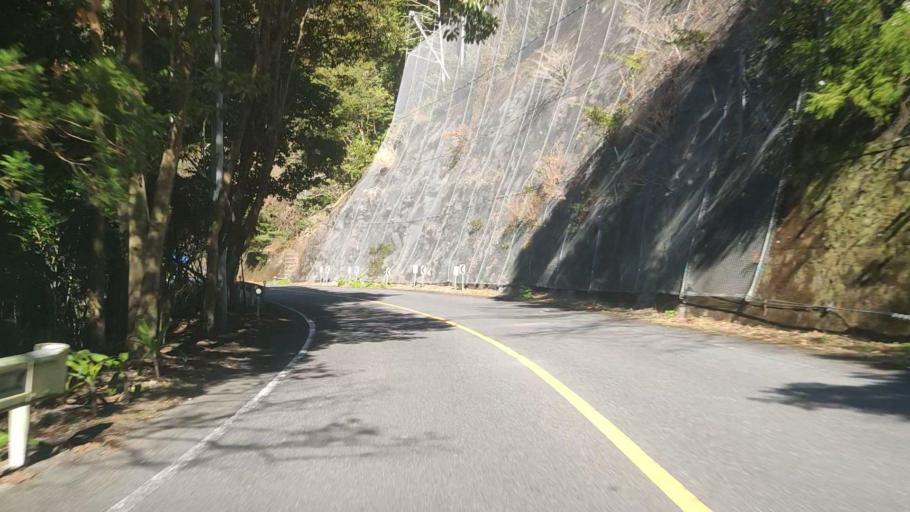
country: JP
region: Oita
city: Saiki
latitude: 32.8789
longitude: 131.9489
